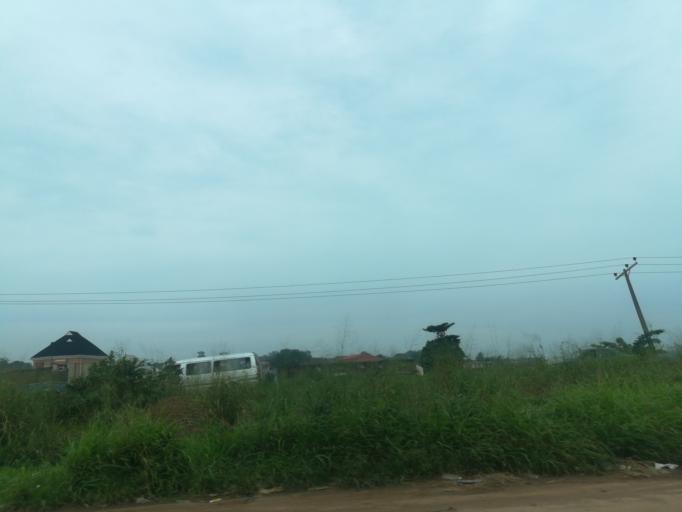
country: NG
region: Oyo
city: Egbeda
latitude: 7.3818
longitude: 3.9951
